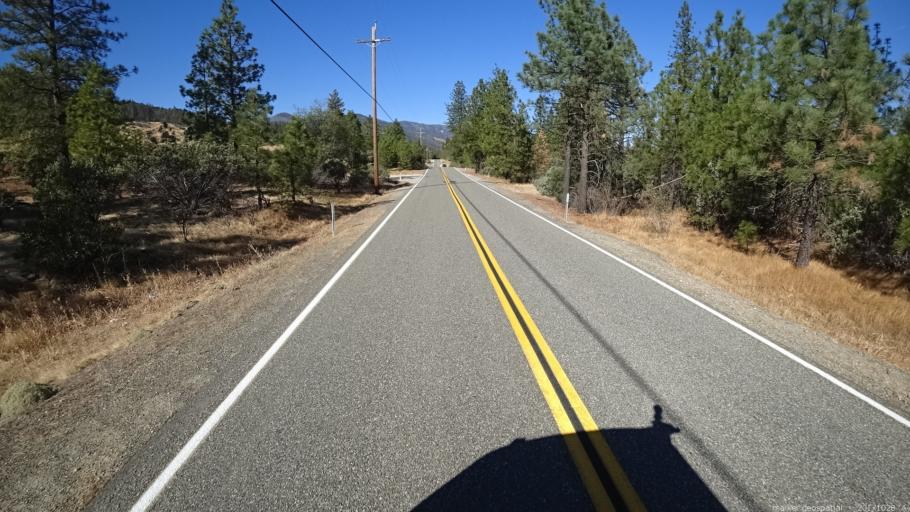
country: US
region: California
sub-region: Shasta County
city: Shasta
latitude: 40.6425
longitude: -122.4572
